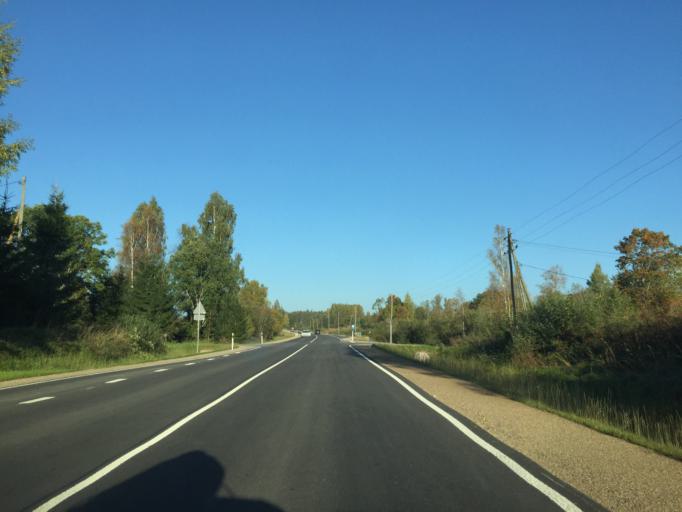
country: LV
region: Vecpiebalga
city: Vecpiebalga
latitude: 57.1058
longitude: 25.7139
